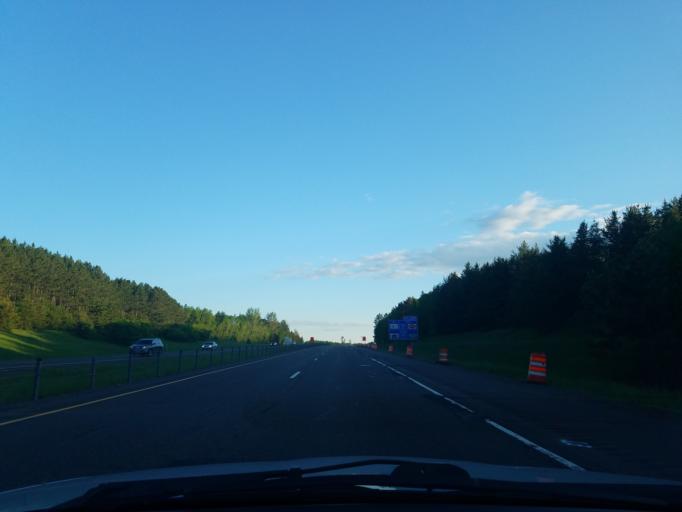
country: US
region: Minnesota
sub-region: Carlton County
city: Carlton
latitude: 46.6775
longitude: -92.4630
